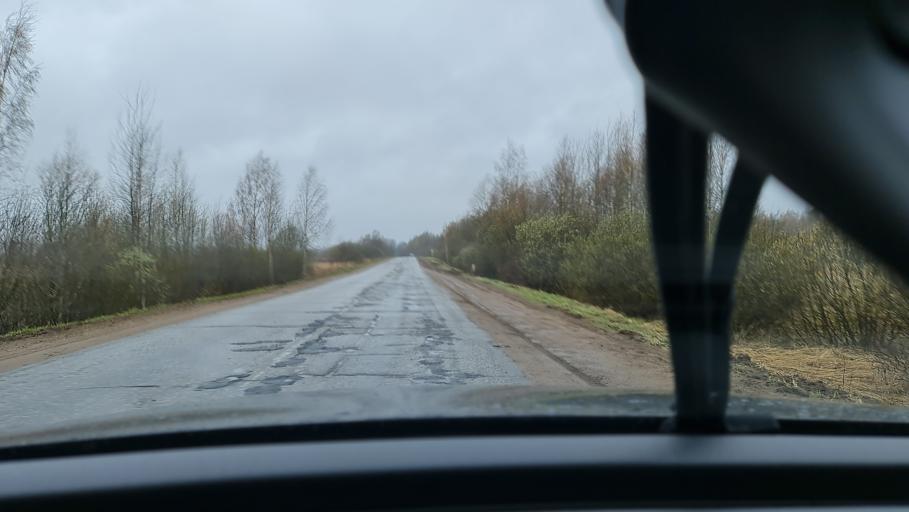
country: RU
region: Novgorod
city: Kresttsy
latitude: 58.0089
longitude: 32.7732
